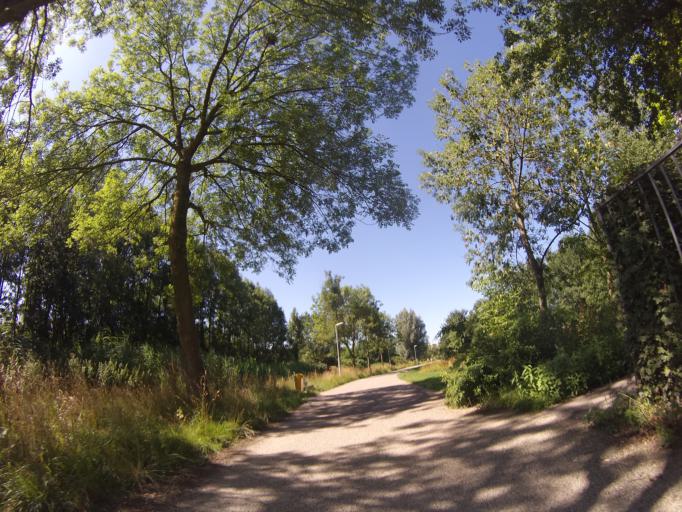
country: NL
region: Utrecht
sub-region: Gemeente Utrecht
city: Utrecht
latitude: 52.1127
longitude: 5.1345
